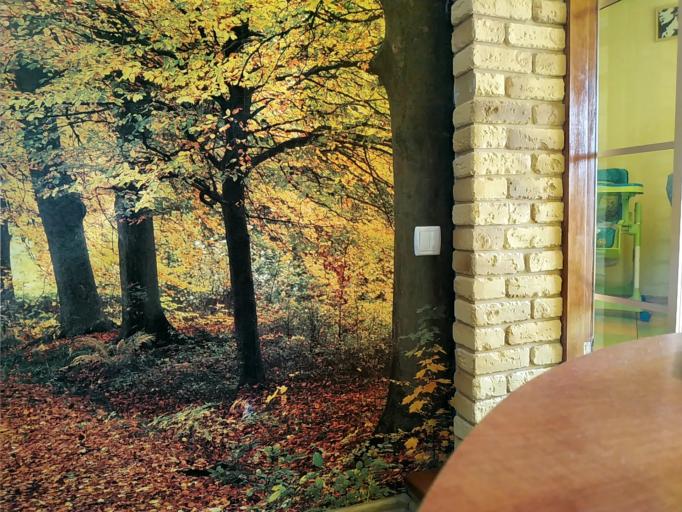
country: RU
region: Novgorod
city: Parfino
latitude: 57.8063
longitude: 31.5892
